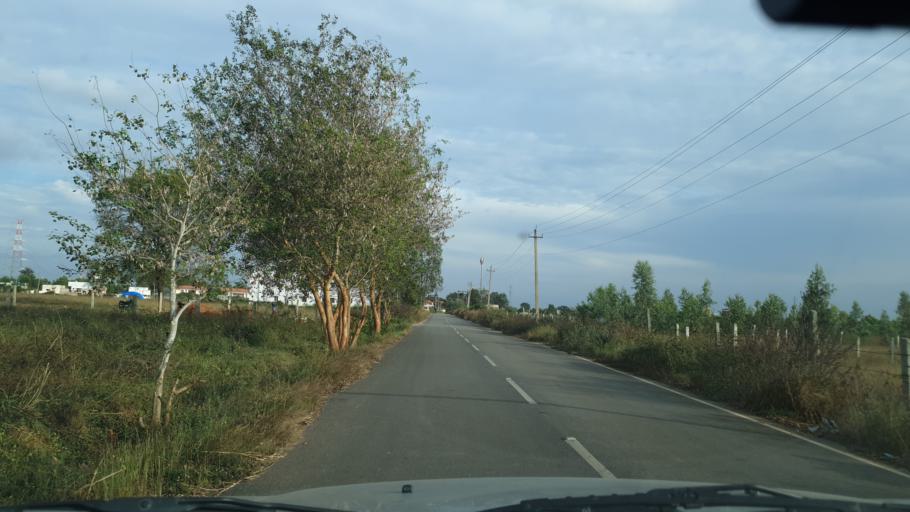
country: IN
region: Karnataka
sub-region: Bangalore Urban
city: Yelahanka
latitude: 13.1955
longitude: 77.6202
